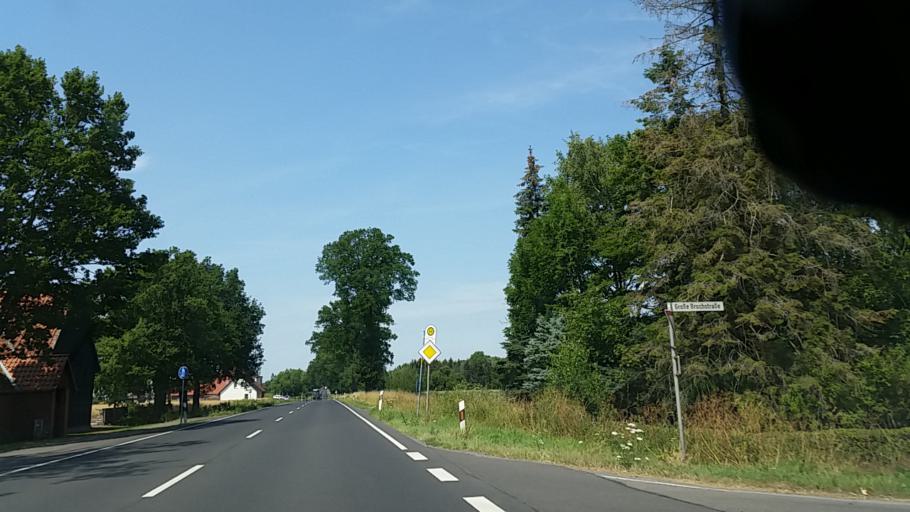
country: DE
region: Lower Saxony
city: Wietzen
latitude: 52.6981
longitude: 9.0858
